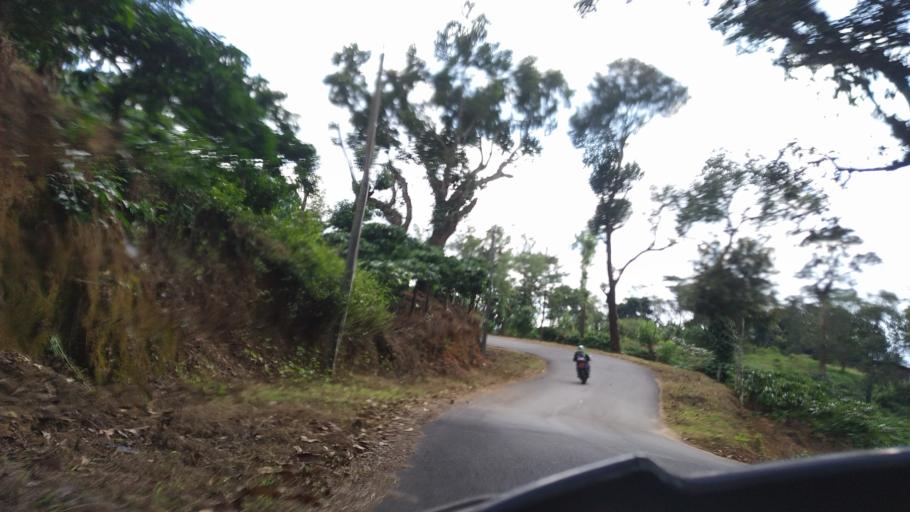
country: IN
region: Karnataka
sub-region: Kodagu
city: Ponnampet
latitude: 12.0314
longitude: 75.9208
